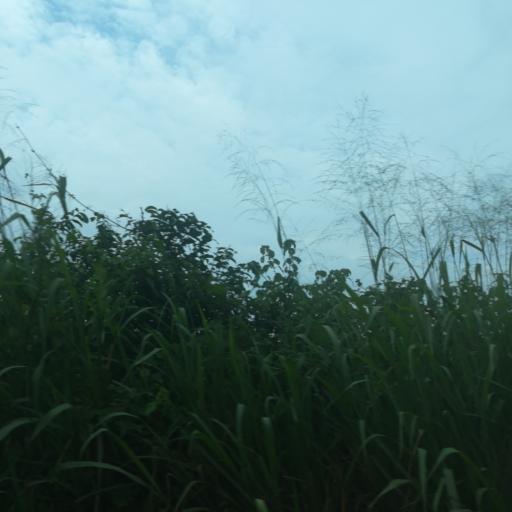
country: NG
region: Lagos
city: Ejirin
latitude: 6.6474
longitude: 3.7671
